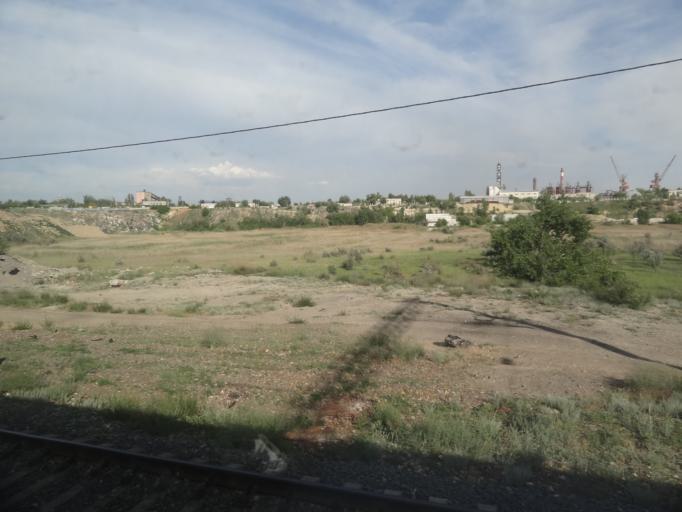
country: RU
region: Volgograd
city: Gorodishche
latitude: 48.7794
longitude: 44.4681
